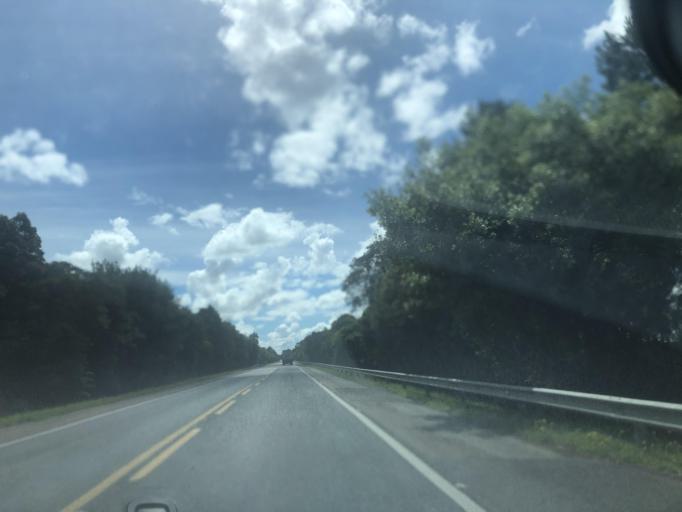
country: BR
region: Santa Catarina
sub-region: Tres Barras
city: Tres Barras
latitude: -26.3373
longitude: -50.0761
